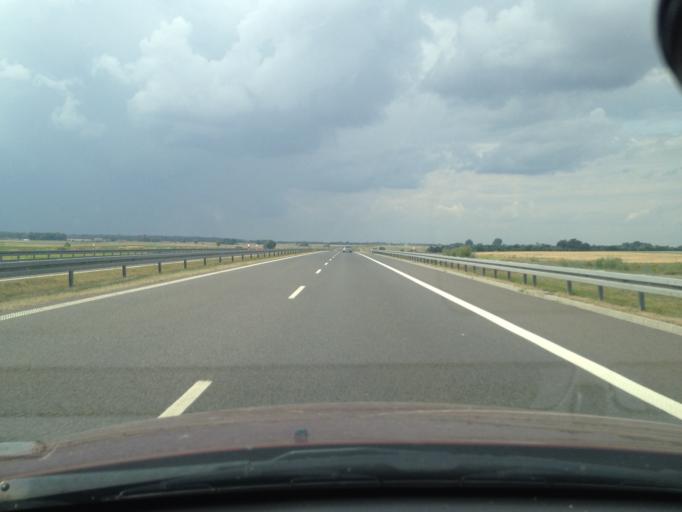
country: PL
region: West Pomeranian Voivodeship
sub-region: Powiat pyrzycki
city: Kozielice
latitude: 53.0993
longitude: 14.7996
